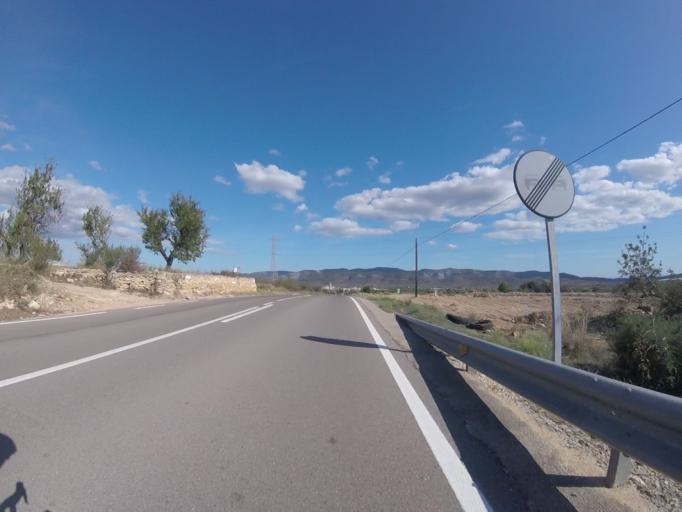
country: ES
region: Valencia
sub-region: Provincia de Castello
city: Alcala de Xivert
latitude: 40.3023
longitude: 0.1978
